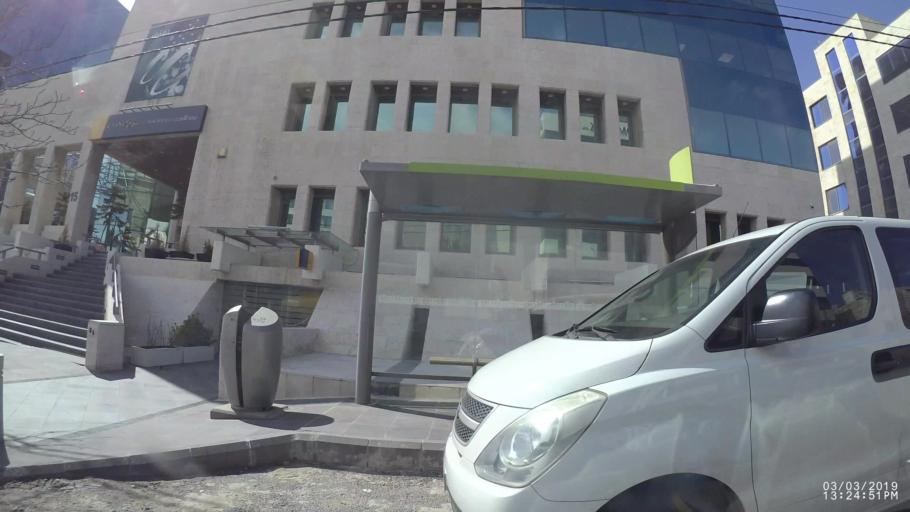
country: JO
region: Amman
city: Amman
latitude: 31.9685
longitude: 35.8961
